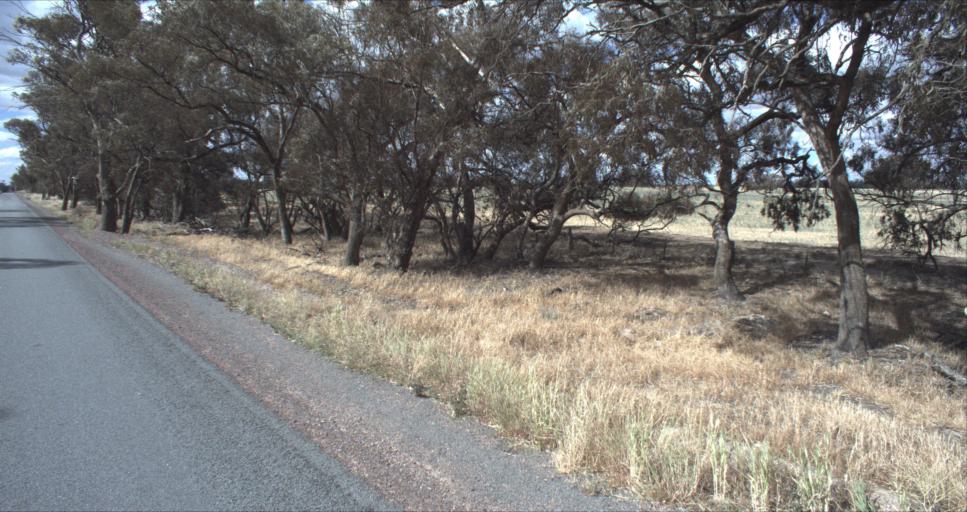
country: AU
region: New South Wales
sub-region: Leeton
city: Leeton
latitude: -34.6777
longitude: 146.3462
